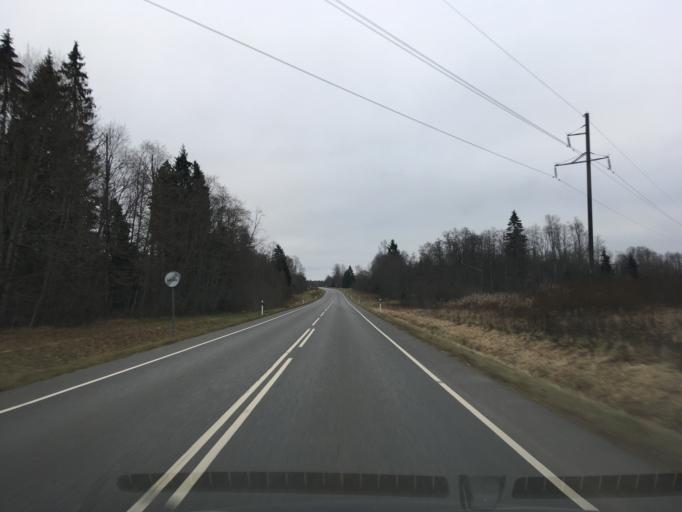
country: EE
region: Laeaene-Virumaa
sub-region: Kadrina vald
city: Kadrina
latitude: 59.4519
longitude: 26.0337
